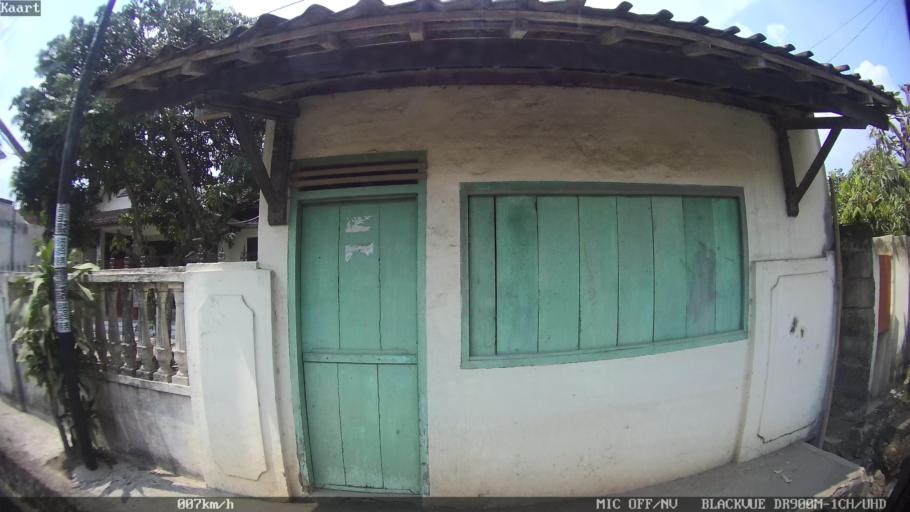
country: ID
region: Lampung
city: Pringsewu
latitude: -5.3578
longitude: 104.9782
